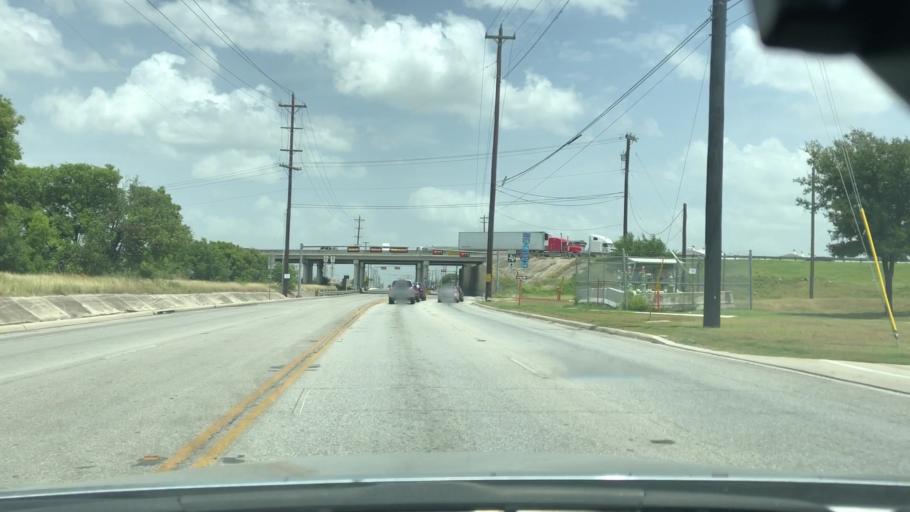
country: US
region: Texas
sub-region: Bexar County
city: Kirby
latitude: 29.4588
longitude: -98.4055
